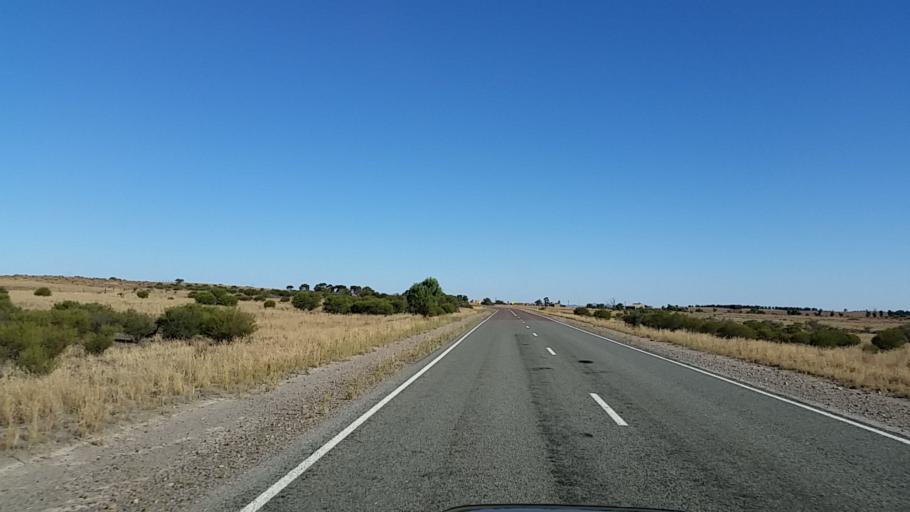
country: AU
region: South Australia
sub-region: Peterborough
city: Peterborough
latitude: -32.5480
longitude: 138.5603
